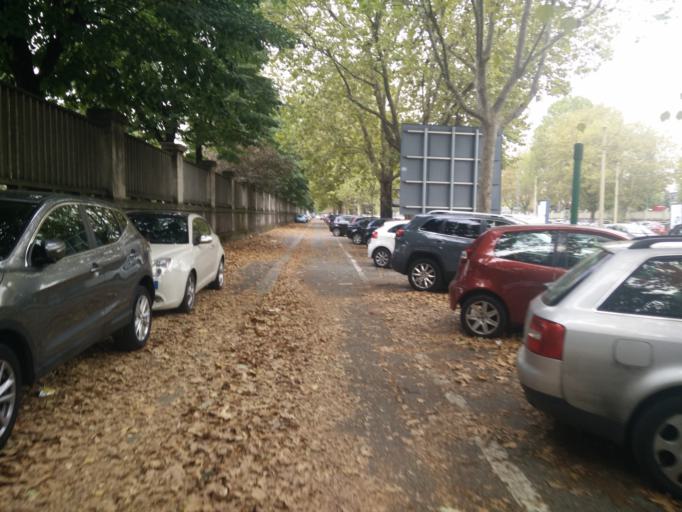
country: IT
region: Piedmont
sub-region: Provincia di Torino
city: Gerbido
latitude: 45.0230
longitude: 7.6341
